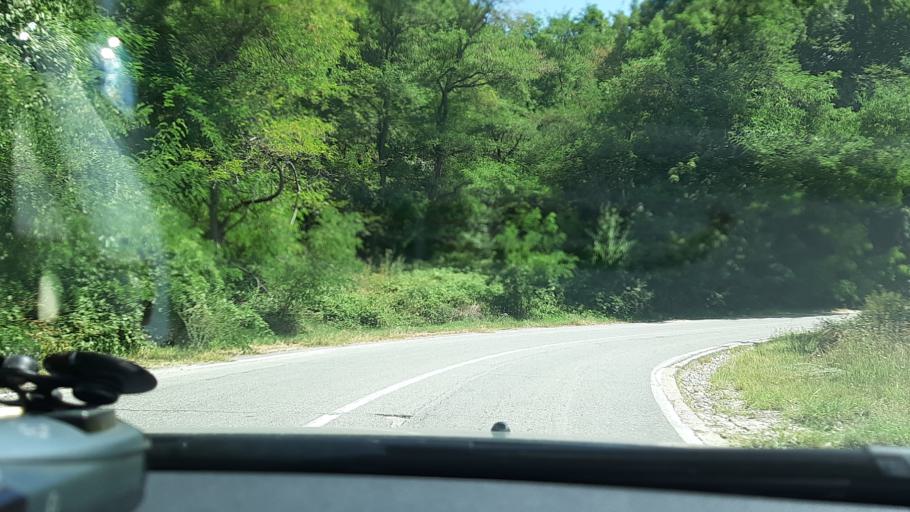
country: RO
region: Gorj
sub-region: Comuna Logresti-Mosteni
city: Logresti Mosteni
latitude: 44.9129
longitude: 23.7634
